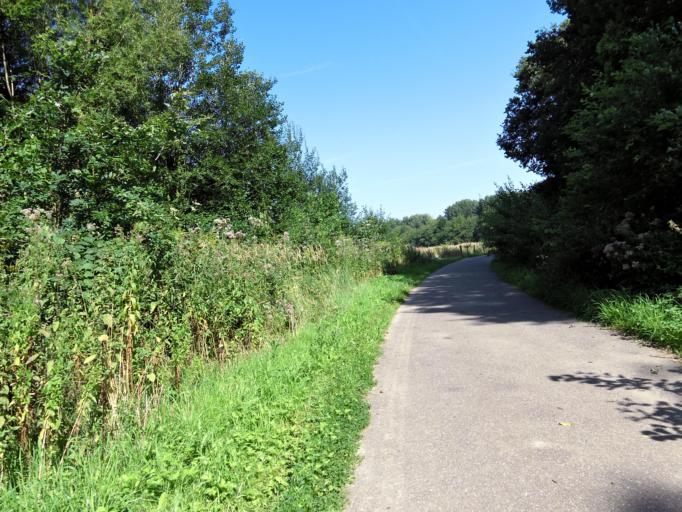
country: NL
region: Limburg
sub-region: Gemeente Voerendaal
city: Voerendaal
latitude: 50.8920
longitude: 5.9402
